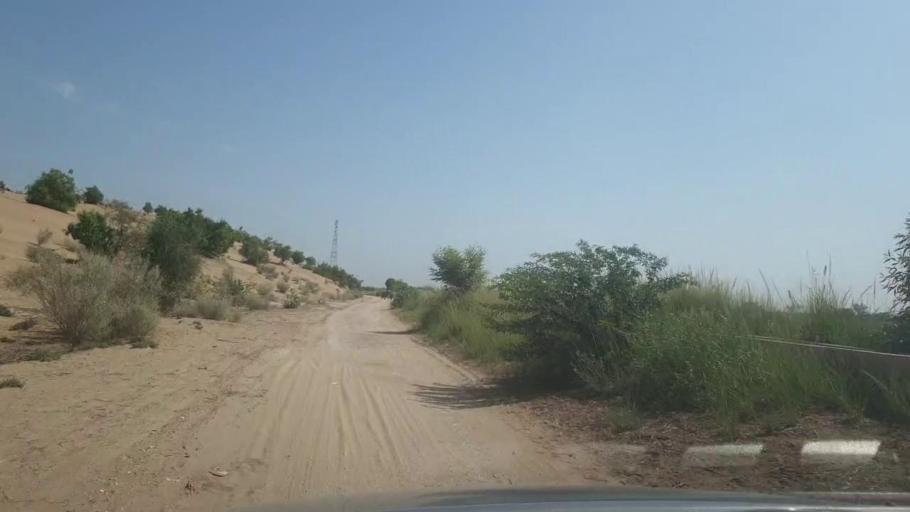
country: PK
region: Sindh
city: Khairpur
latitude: 27.3952
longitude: 69.0776
